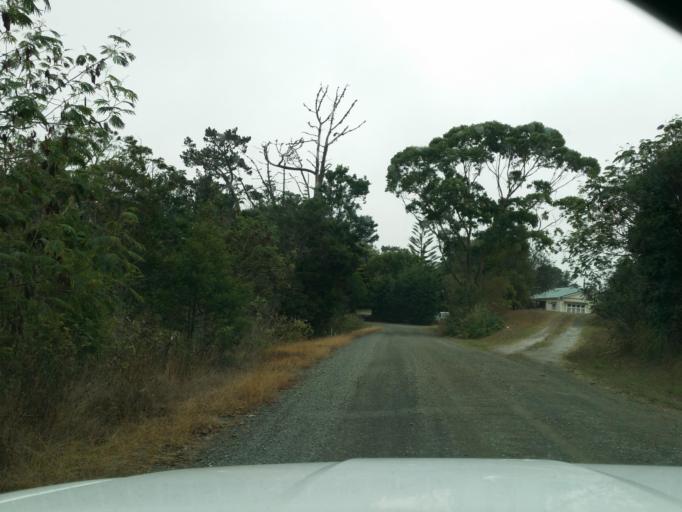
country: NZ
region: Northland
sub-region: Kaipara District
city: Dargaville
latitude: -35.9640
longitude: 173.8621
